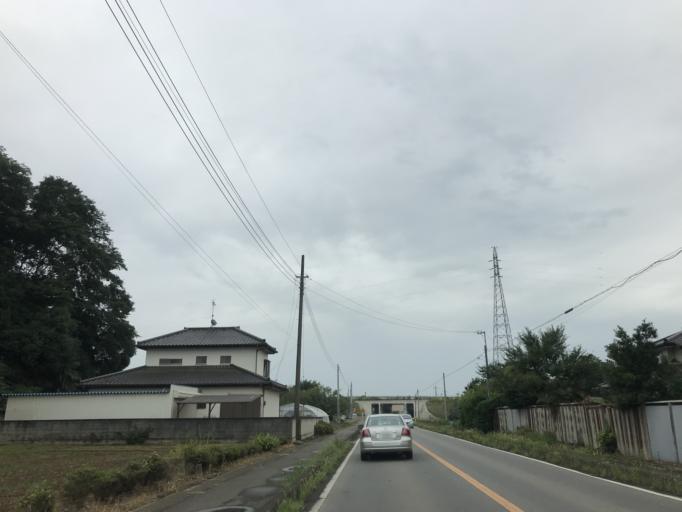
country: JP
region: Ibaraki
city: Sakai
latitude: 36.1300
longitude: 139.7943
